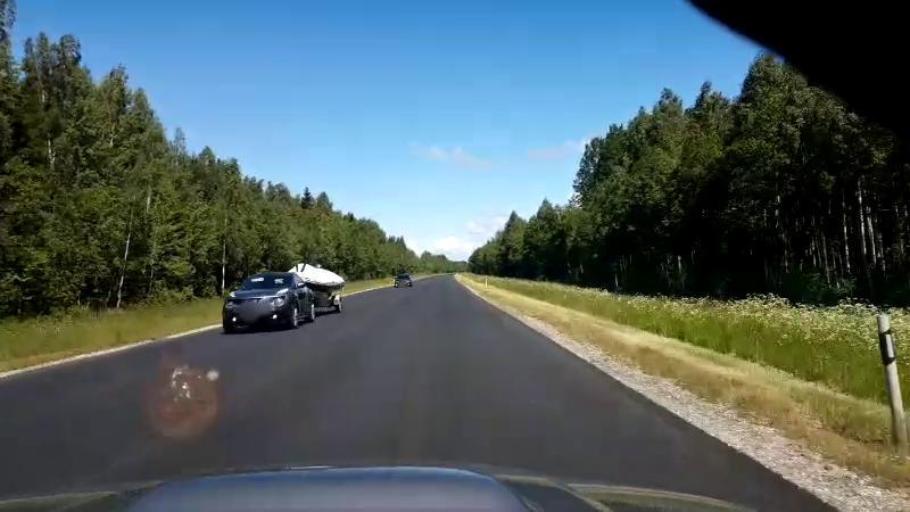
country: LV
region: Salacgrivas
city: Ainazi
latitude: 57.9380
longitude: 24.4299
